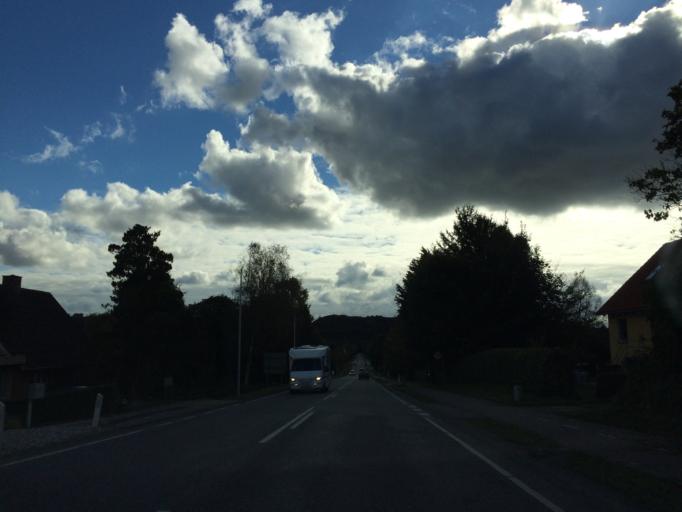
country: DK
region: Central Jutland
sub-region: Skanderborg Kommune
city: Ry
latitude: 56.1073
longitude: 9.7846
